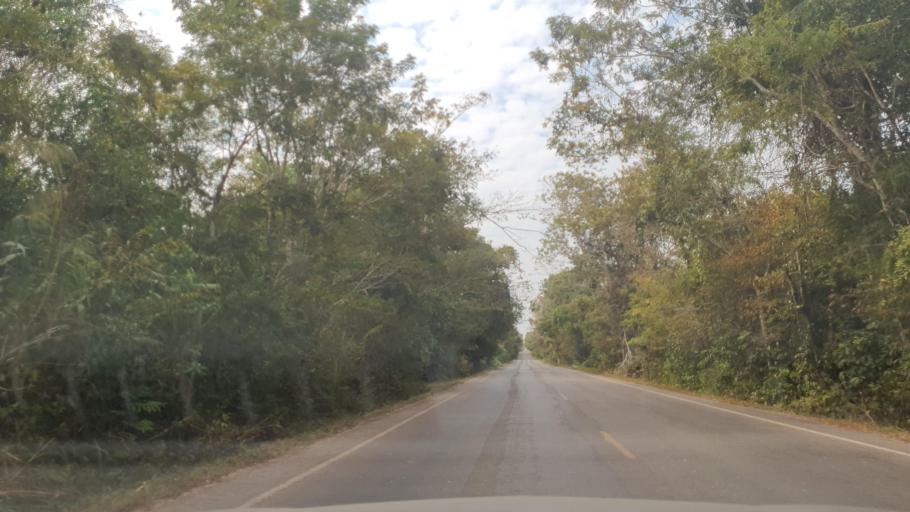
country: TH
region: Changwat Bueng Kan
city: Bung Khla
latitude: 18.2963
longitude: 103.9329
